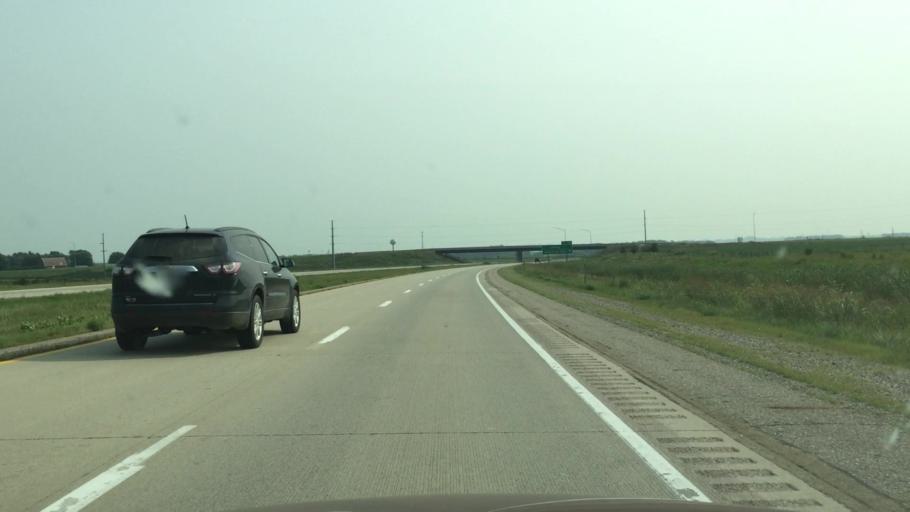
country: US
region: Iowa
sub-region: Osceola County
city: Sibley
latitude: 43.3797
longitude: -95.7553
